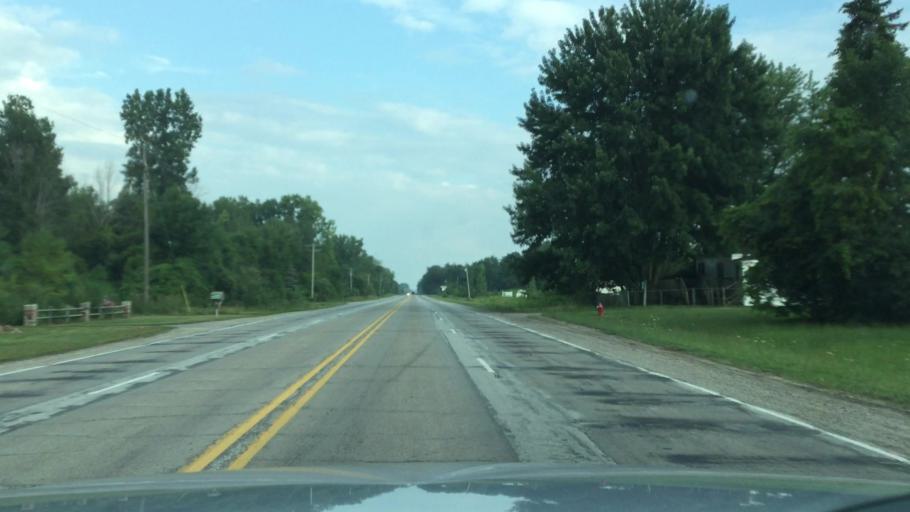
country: US
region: Michigan
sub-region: Saginaw County
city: Birch Run
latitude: 43.2831
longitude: -83.7943
